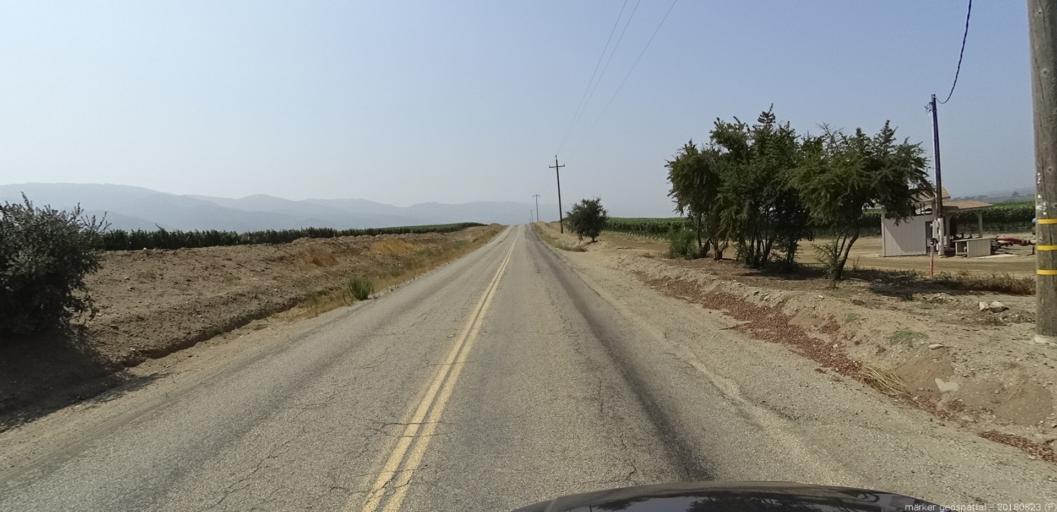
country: US
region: California
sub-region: Monterey County
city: Soledad
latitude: 36.4284
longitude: -121.4058
